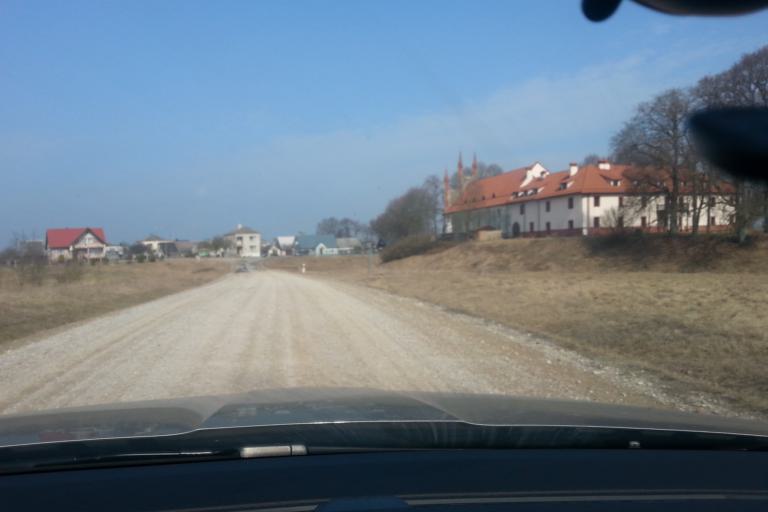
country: LT
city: Trakai
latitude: 54.6041
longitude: 24.9830
